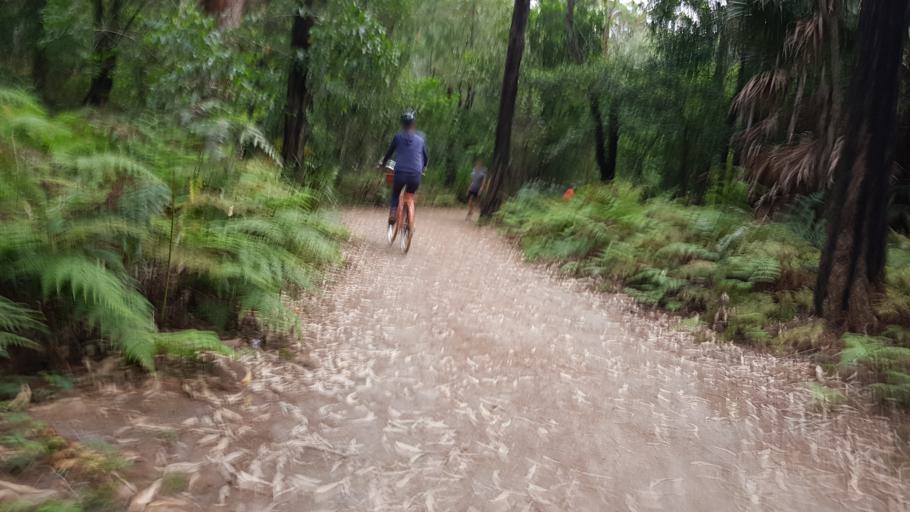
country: AU
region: New South Wales
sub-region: Warringah
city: Narrabeen
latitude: -33.7188
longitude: 151.2800
